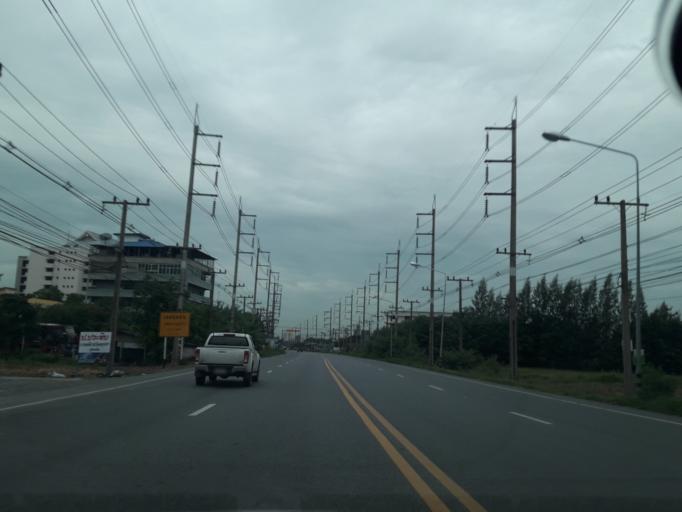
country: TH
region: Pathum Thani
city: Ban Lam Luk Ka
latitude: 13.9496
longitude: 100.8015
